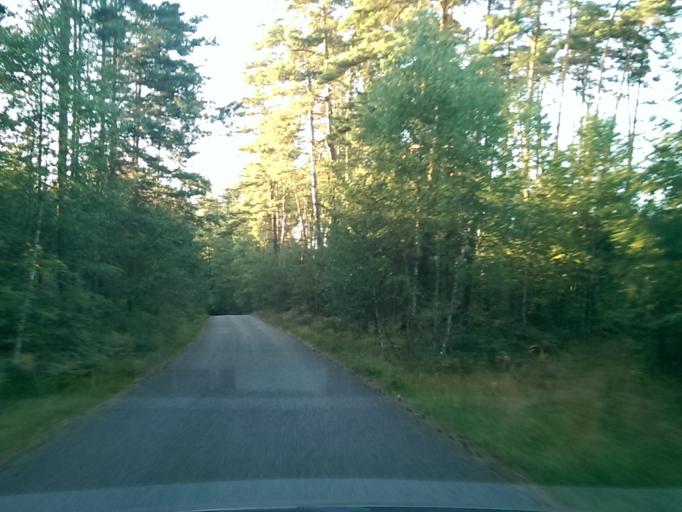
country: CZ
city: Doksy
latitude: 50.5091
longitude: 14.7006
